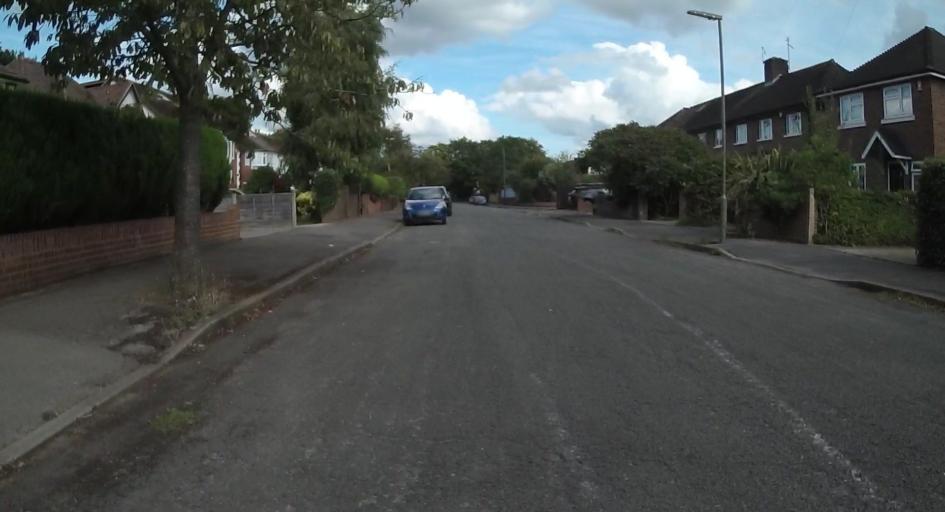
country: GB
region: England
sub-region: Surrey
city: Walton-on-Thames
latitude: 51.3815
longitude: -0.4009
